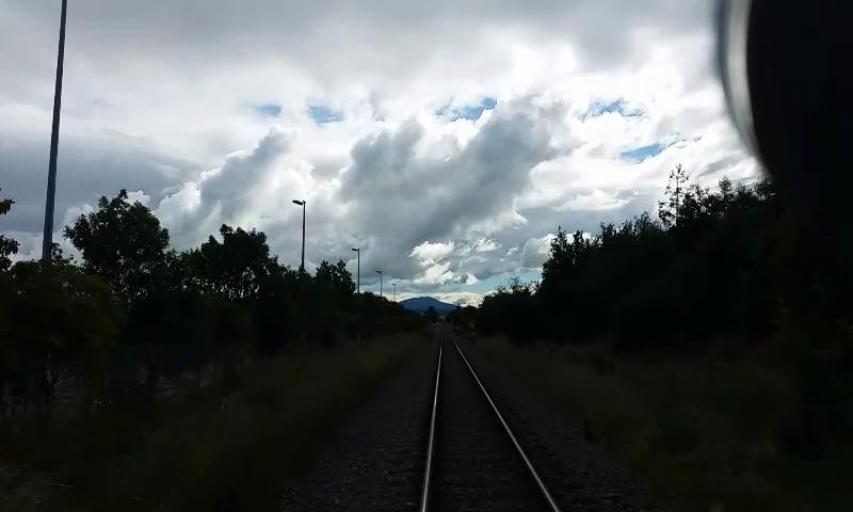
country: NZ
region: Canterbury
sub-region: Waimakariri District
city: Woodend
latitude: -43.3127
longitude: 172.6005
